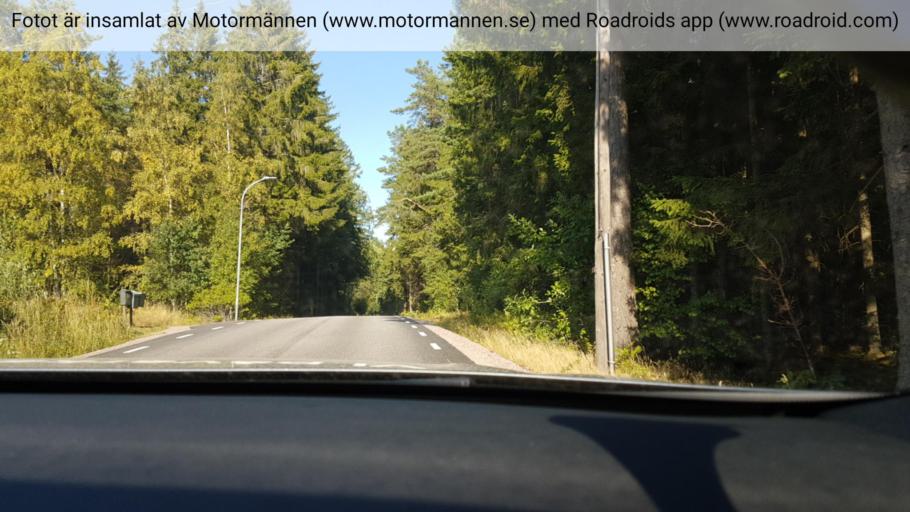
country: SE
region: Vaestra Goetaland
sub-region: Gotene Kommun
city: Goetene
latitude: 58.6223
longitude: 13.6135
